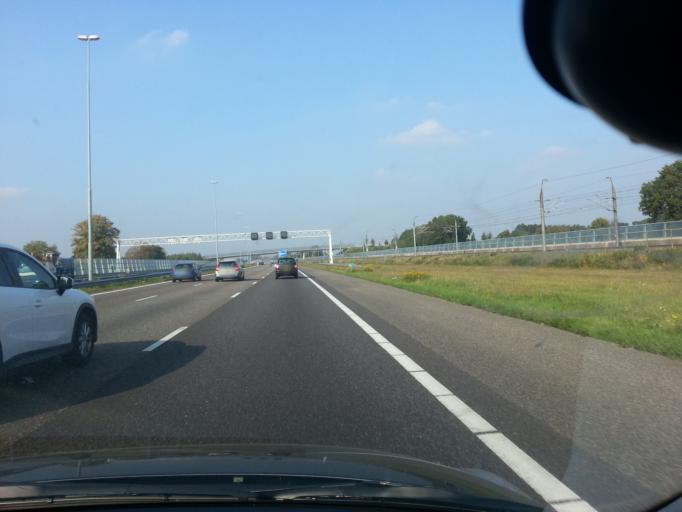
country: NL
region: North Brabant
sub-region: Gemeente Breda
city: Breda
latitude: 51.5434
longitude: 4.7405
